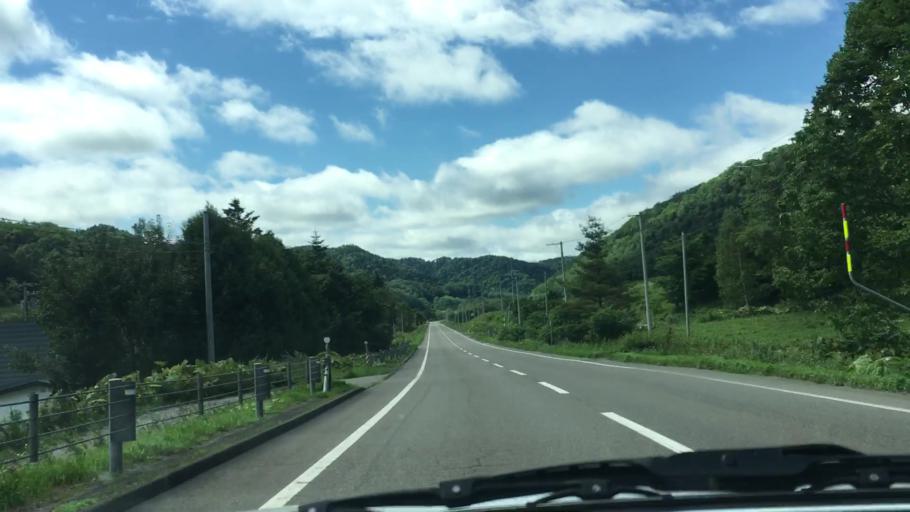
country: JP
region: Hokkaido
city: Kitami
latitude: 43.3678
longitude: 143.8615
